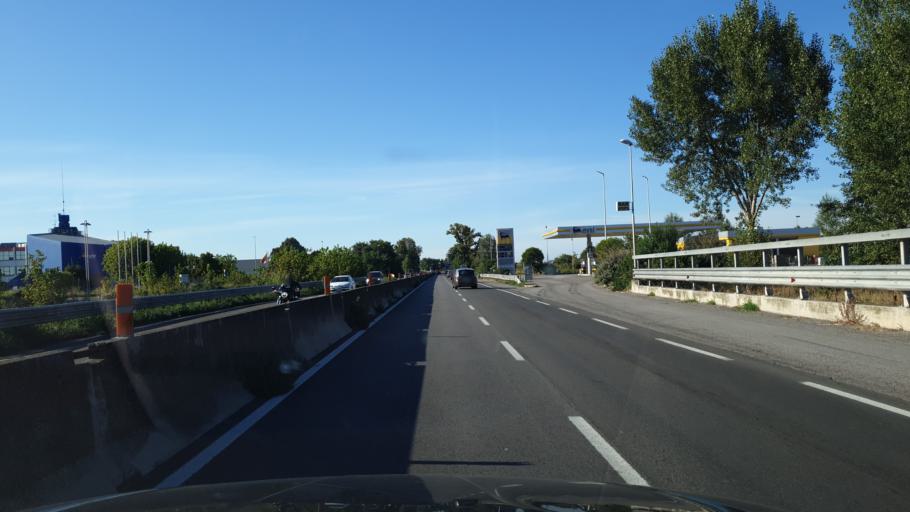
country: IT
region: Emilia-Romagna
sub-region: Provincia di Ravenna
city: Ravenna
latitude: 44.4141
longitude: 12.1703
